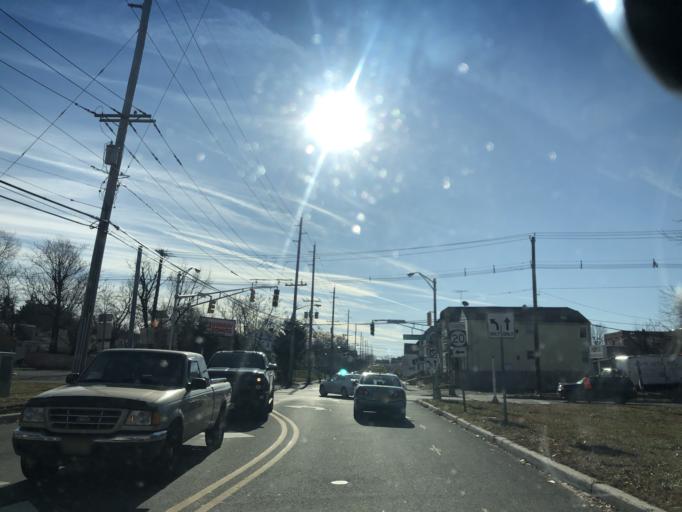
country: US
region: New Jersey
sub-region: Bergen County
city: Fair Lawn
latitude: 40.9230
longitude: -74.1409
